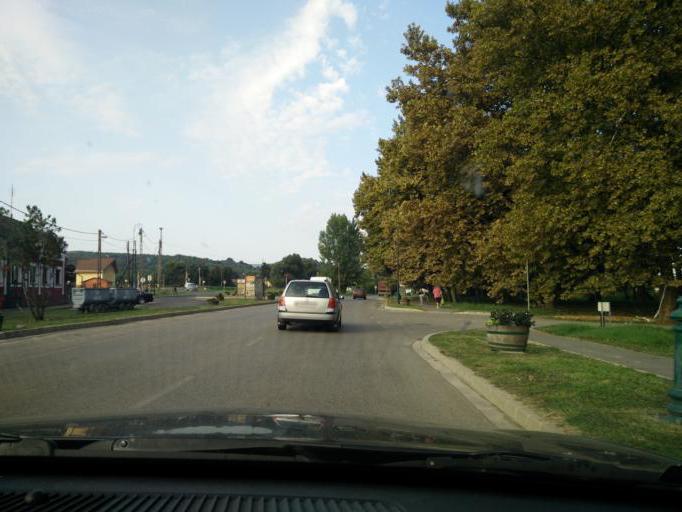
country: HU
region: Tolna
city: Nagymanyok
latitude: 46.2804
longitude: 18.4578
